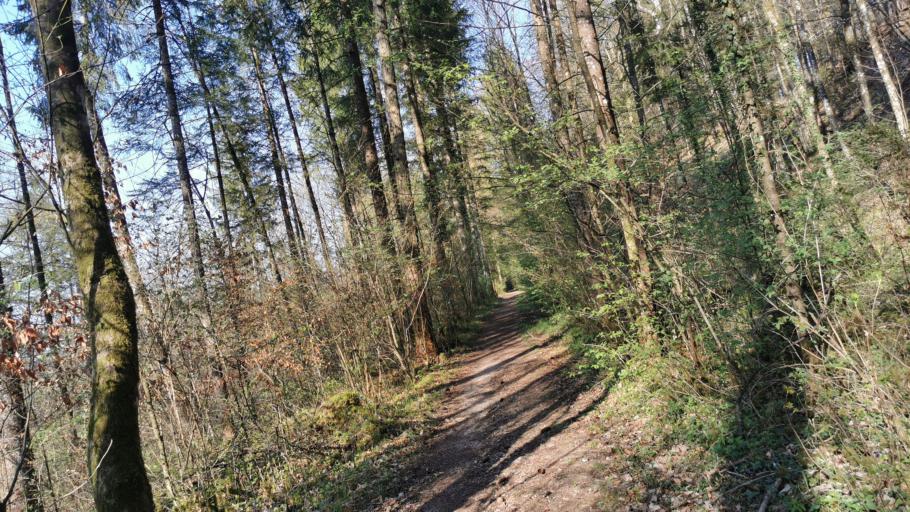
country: AT
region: Salzburg
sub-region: Politischer Bezirk Salzburg-Umgebung
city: Grodig
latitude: 47.7459
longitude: 12.9989
